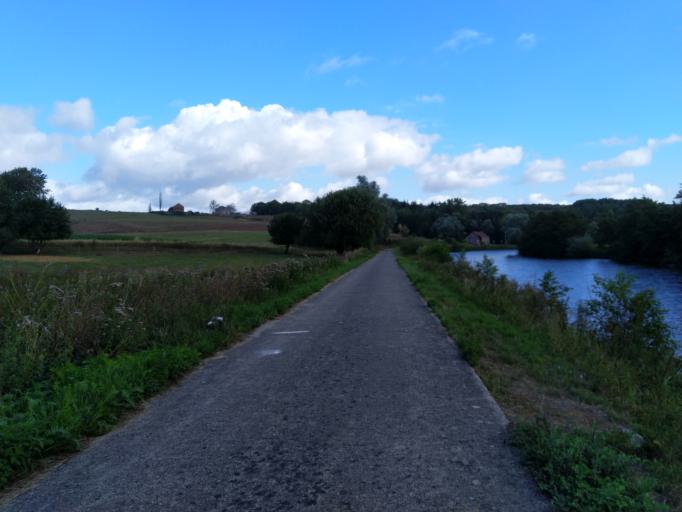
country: BE
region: Wallonia
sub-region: Province du Hainaut
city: Merbes-le-Chateau
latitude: 50.3240
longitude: 4.2097
